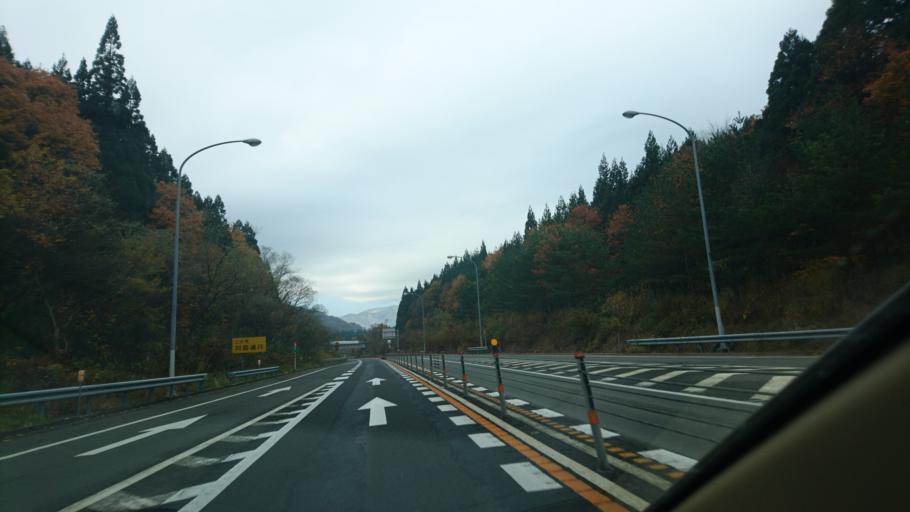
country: JP
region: Iwate
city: Kitakami
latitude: 39.2924
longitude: 140.9819
